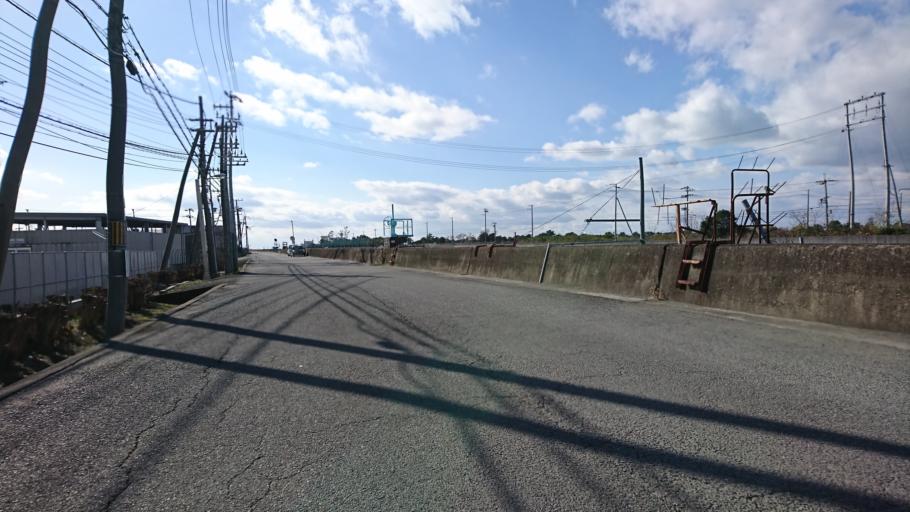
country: JP
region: Hyogo
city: Shirahamacho-usazakiminami
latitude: 34.7708
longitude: 134.7650
